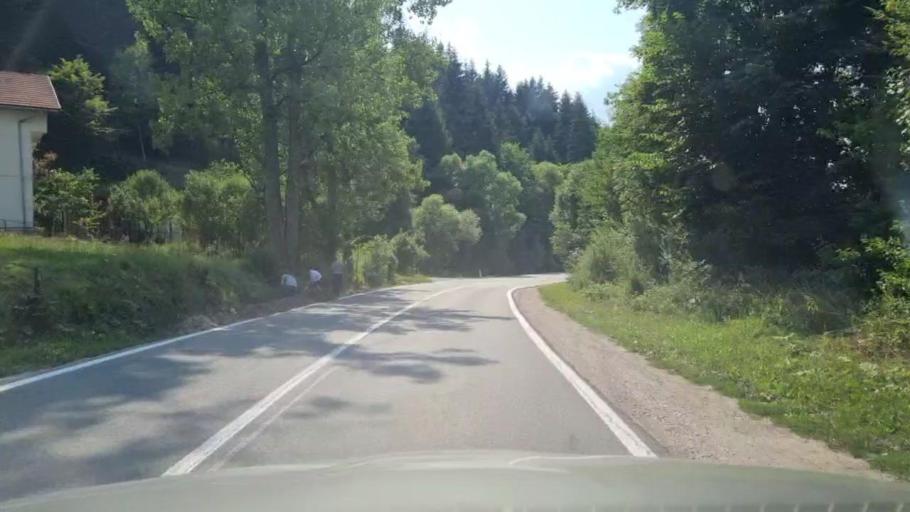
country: BA
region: Federation of Bosnia and Herzegovina
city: Olovo
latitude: 44.1276
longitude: 18.5939
